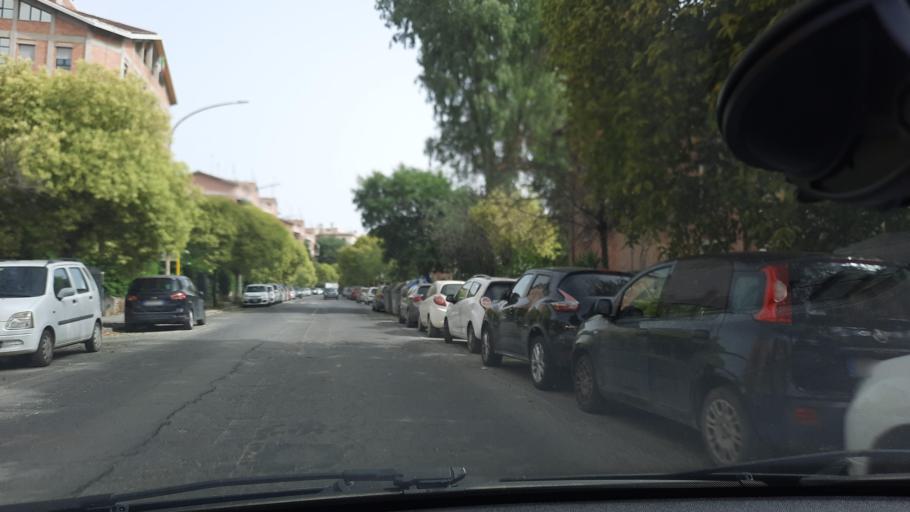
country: IT
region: Latium
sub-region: Citta metropolitana di Roma Capitale
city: Rome
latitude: 41.8643
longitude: 12.4921
